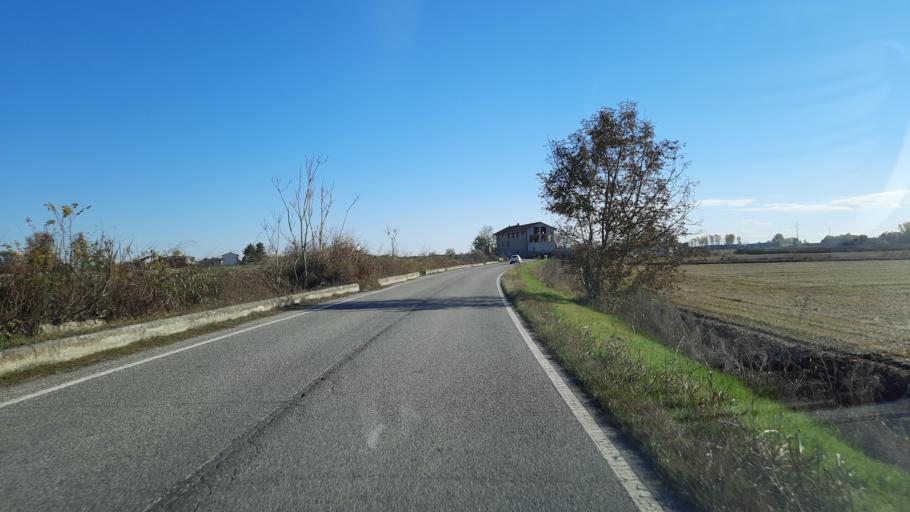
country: IT
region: Piedmont
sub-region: Provincia di Alessandria
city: Villanova Monferrato
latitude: 45.1800
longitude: 8.4605
